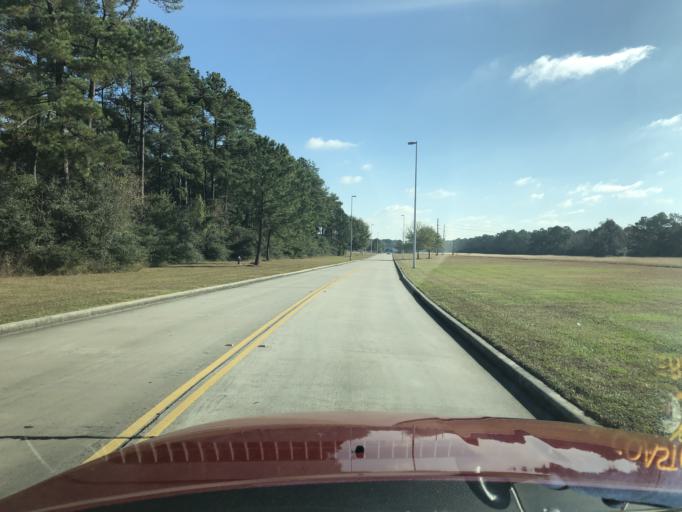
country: US
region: Texas
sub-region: Harris County
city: Aldine
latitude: 29.9666
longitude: -95.3325
